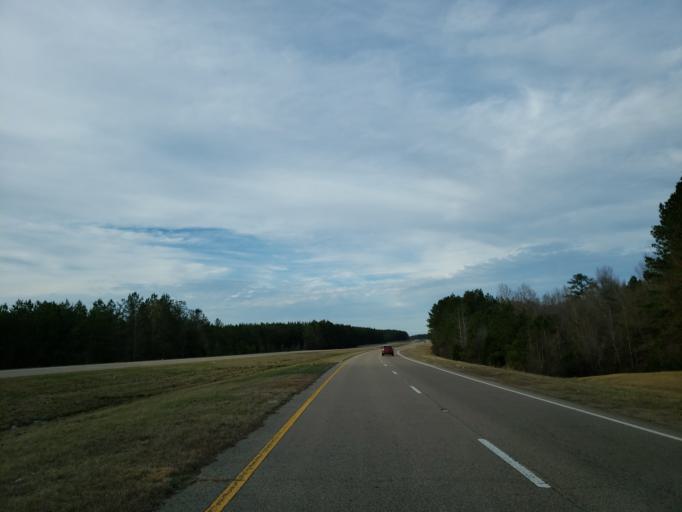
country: US
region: Mississippi
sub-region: Wayne County
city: Waynesboro
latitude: 31.6347
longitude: -88.5932
